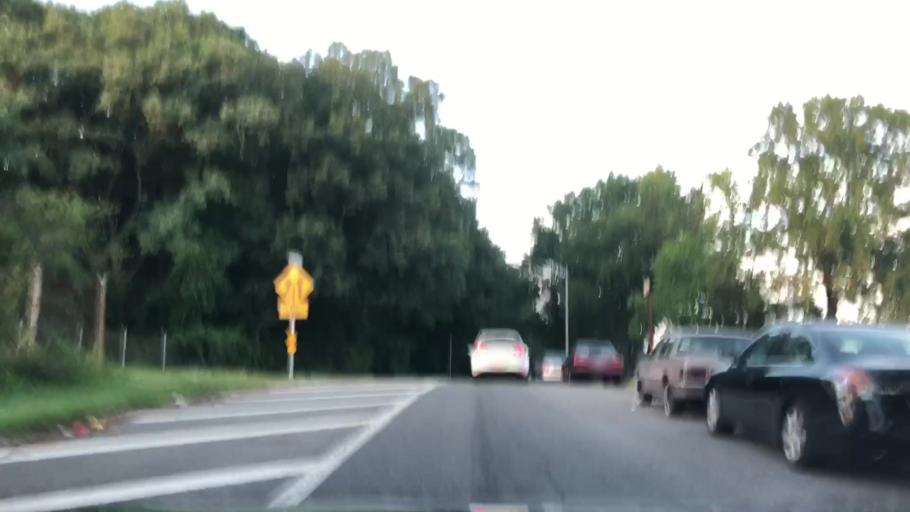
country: US
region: New York
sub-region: Nassau County
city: Bellerose Terrace
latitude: 40.7326
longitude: -73.7455
